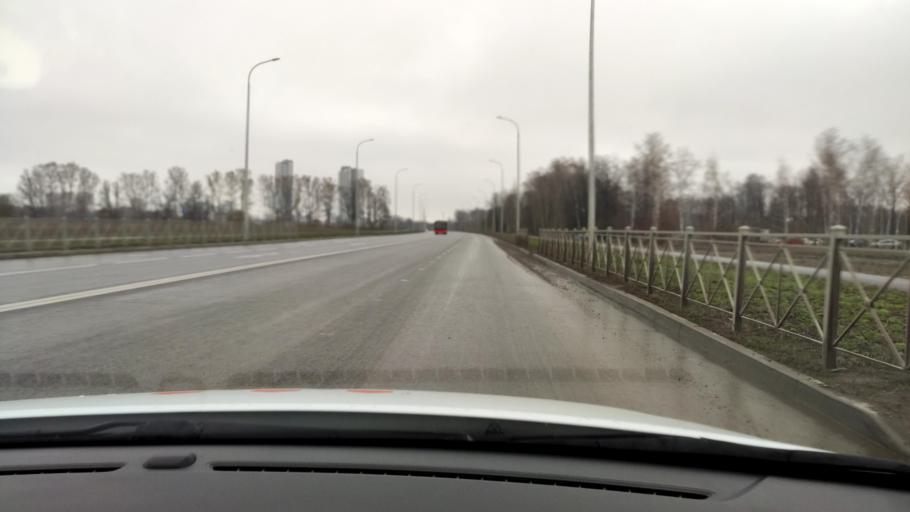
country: RU
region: Tatarstan
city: Stolbishchi
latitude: 55.7162
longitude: 49.1795
